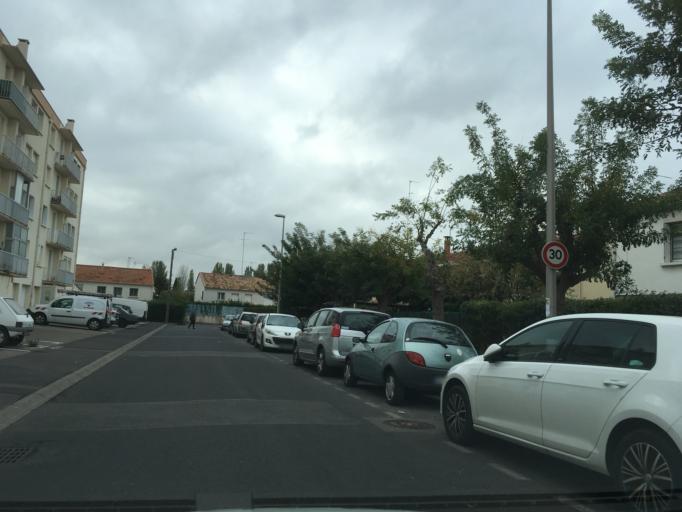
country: FR
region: Languedoc-Roussillon
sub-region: Departement de l'Herault
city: Montpellier
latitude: 43.5933
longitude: 3.8823
